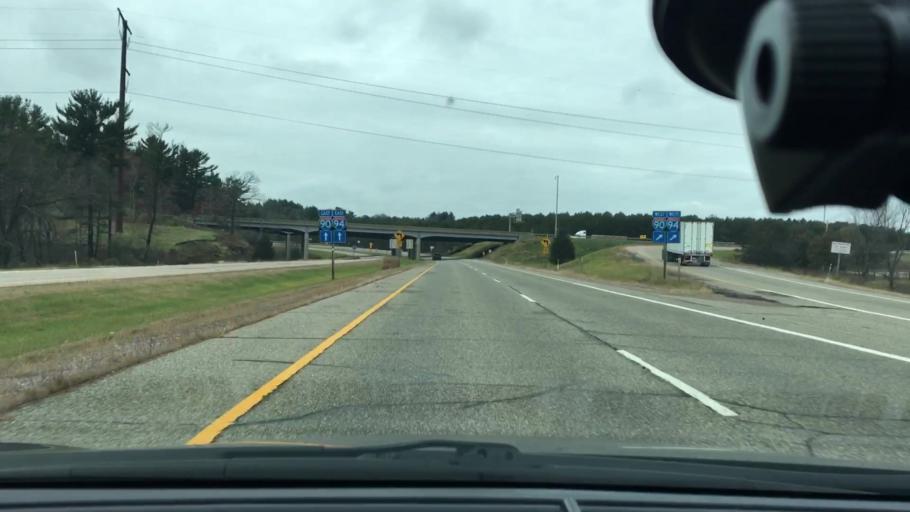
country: US
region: Wisconsin
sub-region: Sauk County
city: Lake Delton
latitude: 43.6245
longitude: -89.8013
